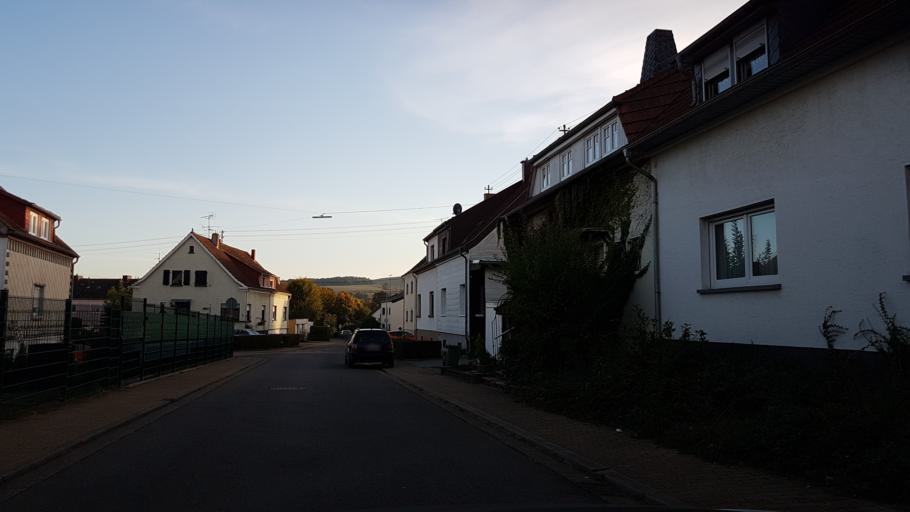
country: DE
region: Saarland
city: Lebach
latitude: 49.4134
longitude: 6.9025
